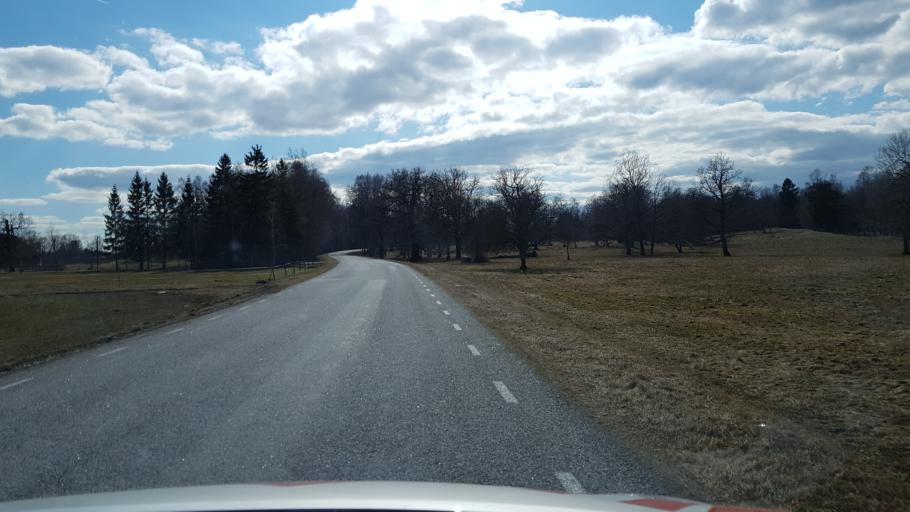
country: EE
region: Laeaene-Virumaa
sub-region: Rakvere linn
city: Rakvere
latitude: 59.3243
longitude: 26.2703
